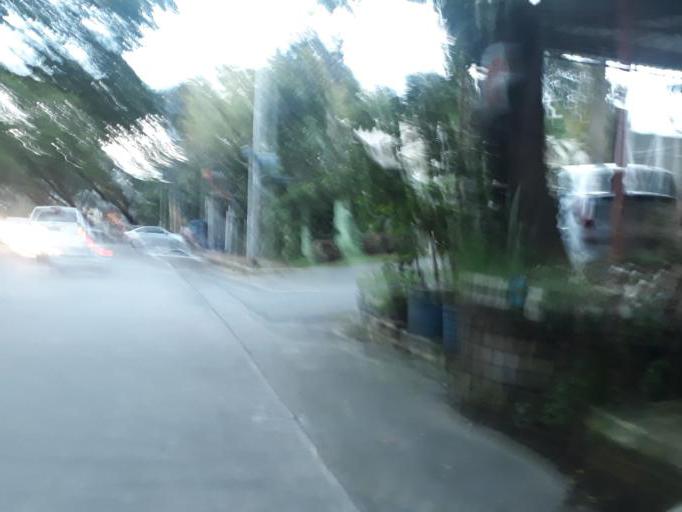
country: PH
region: Metro Manila
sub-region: Quezon City
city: Quezon City
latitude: 14.6858
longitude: 121.0776
